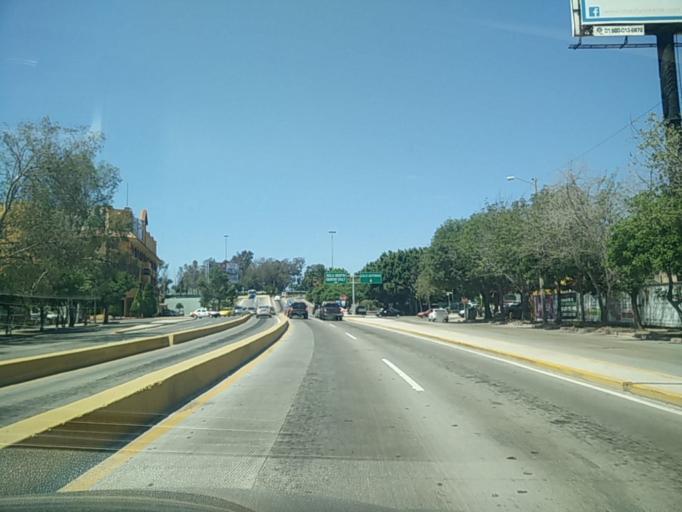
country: MX
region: Baja California
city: Tijuana
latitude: 32.5387
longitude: -117.0234
